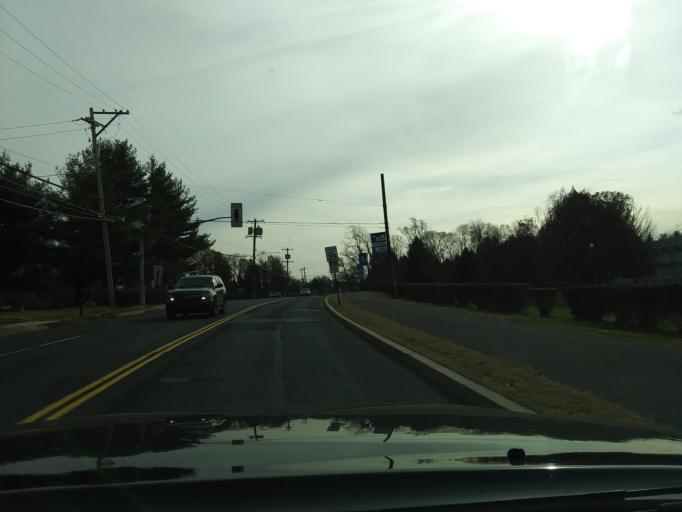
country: US
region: Pennsylvania
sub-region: Montgomery County
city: Rockledge
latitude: 40.0892
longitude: -75.1049
